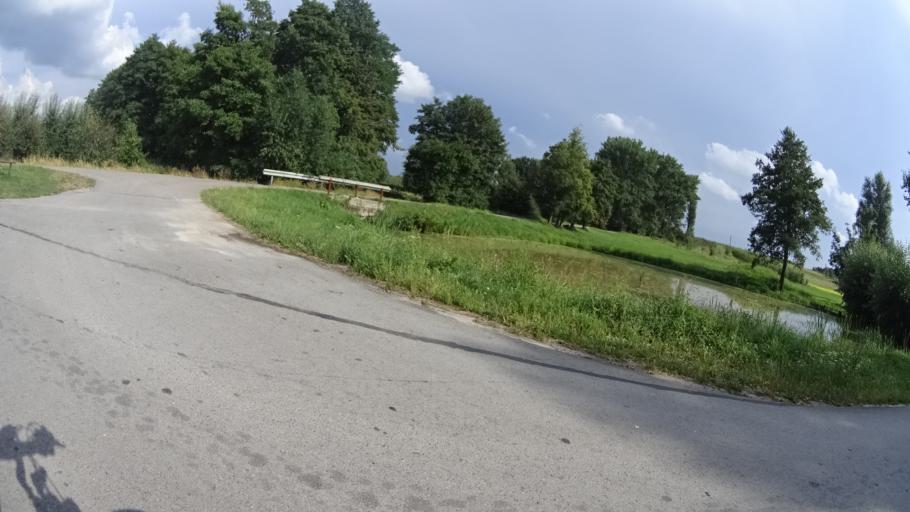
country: PL
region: Masovian Voivodeship
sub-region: Powiat grojecki
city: Goszczyn
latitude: 51.7001
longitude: 20.8470
